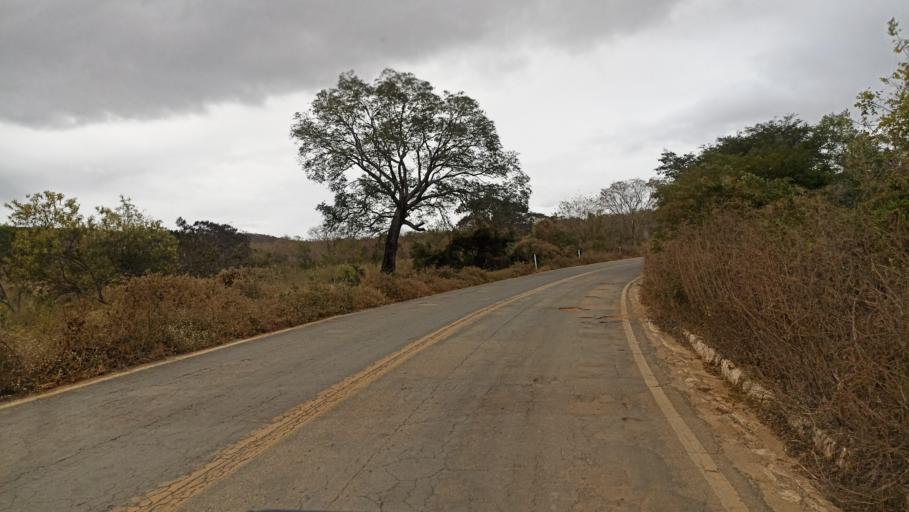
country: BR
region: Minas Gerais
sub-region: Itinga
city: Itinga
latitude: -16.6454
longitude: -41.8286
